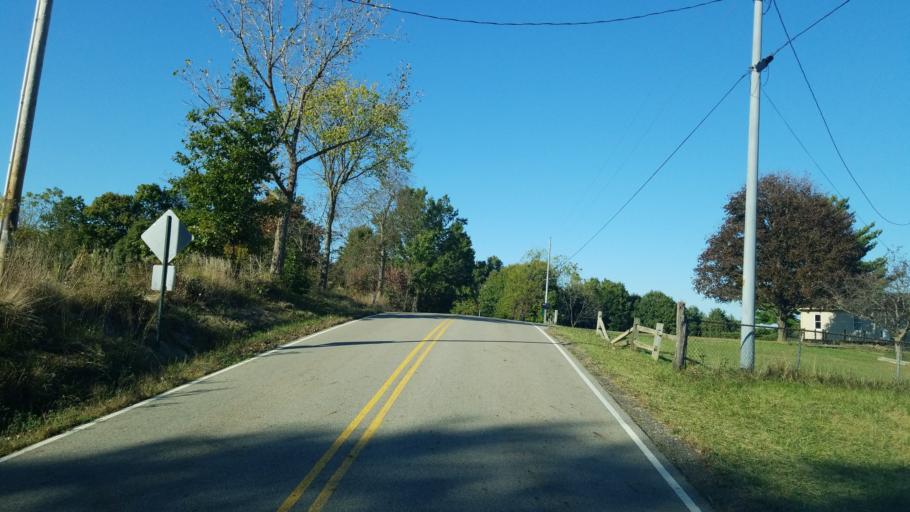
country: US
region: Ohio
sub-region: Licking County
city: Utica
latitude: 40.1682
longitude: -82.3788
